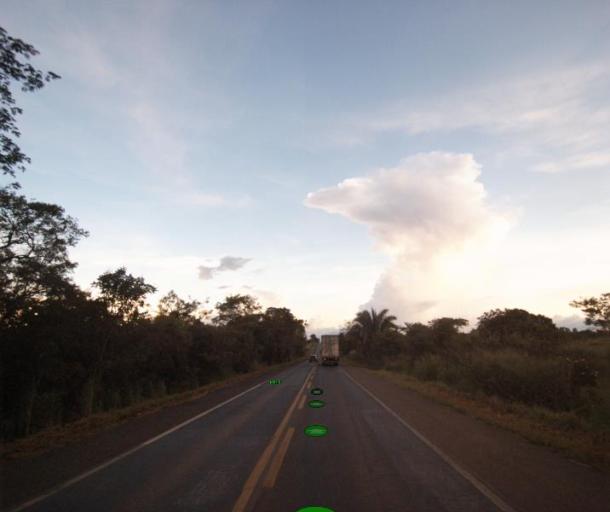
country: BR
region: Goias
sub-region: Uruacu
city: Uruacu
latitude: -14.4508
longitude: -49.1565
